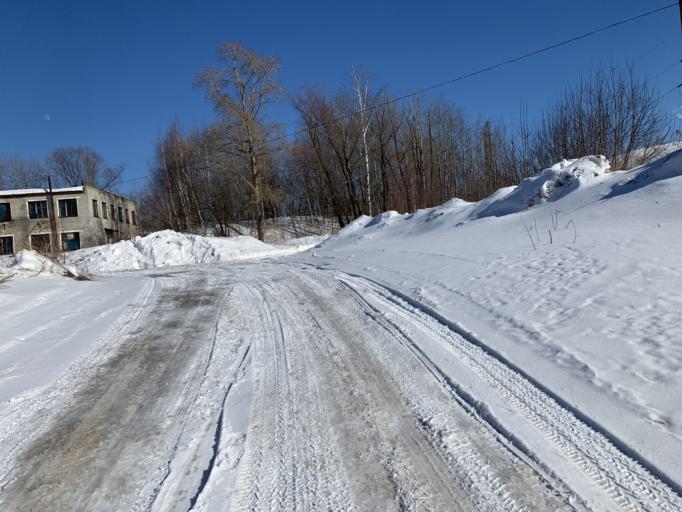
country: RU
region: Chuvashia
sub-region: Cheboksarskiy Rayon
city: Cheboksary
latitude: 56.1389
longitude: 47.2788
